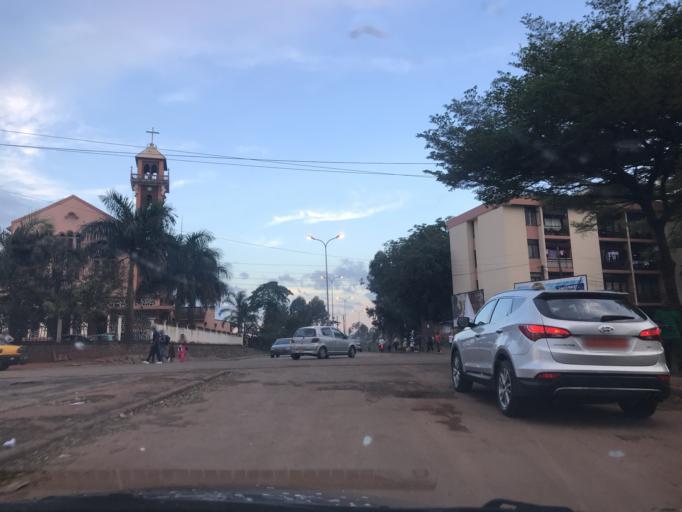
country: CM
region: Centre
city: Yaounde
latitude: 3.8722
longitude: 11.5065
